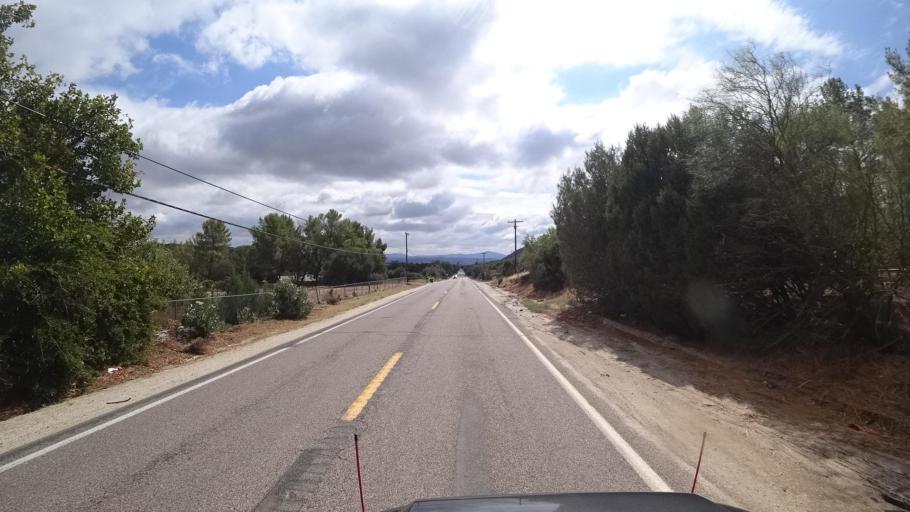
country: US
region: California
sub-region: San Diego County
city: Campo
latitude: 32.6733
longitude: -116.4885
